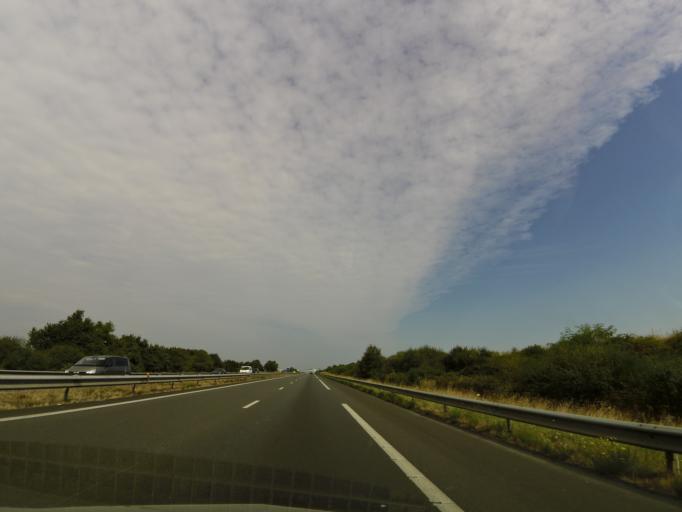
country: FR
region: Pays de la Loire
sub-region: Departement de la Loire-Atlantique
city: Le Bignon
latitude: 47.1226
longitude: -1.4986
